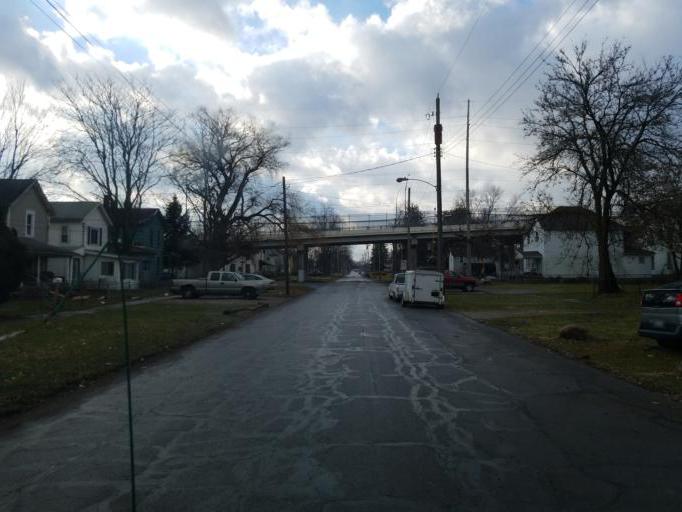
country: US
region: Ohio
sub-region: Marion County
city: Marion
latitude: 40.5852
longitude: -83.1395
